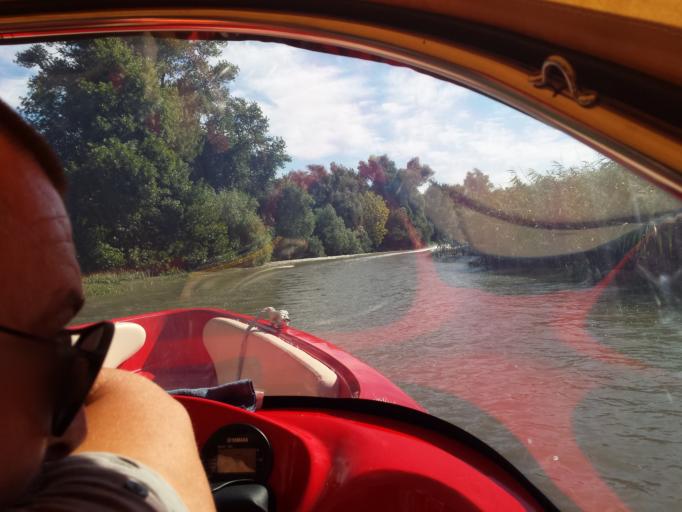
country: RO
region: Tulcea
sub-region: Comuna Pardina
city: Pardina
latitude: 45.2459
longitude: 29.0255
